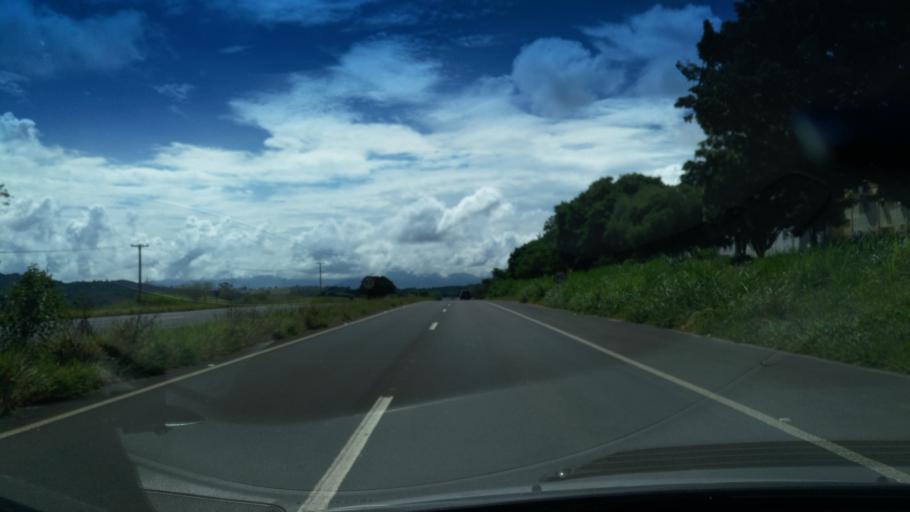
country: BR
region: Sao Paulo
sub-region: Santo Antonio Do Jardim
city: Espirito Santo do Pinhal
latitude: -22.1764
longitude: -46.7496
